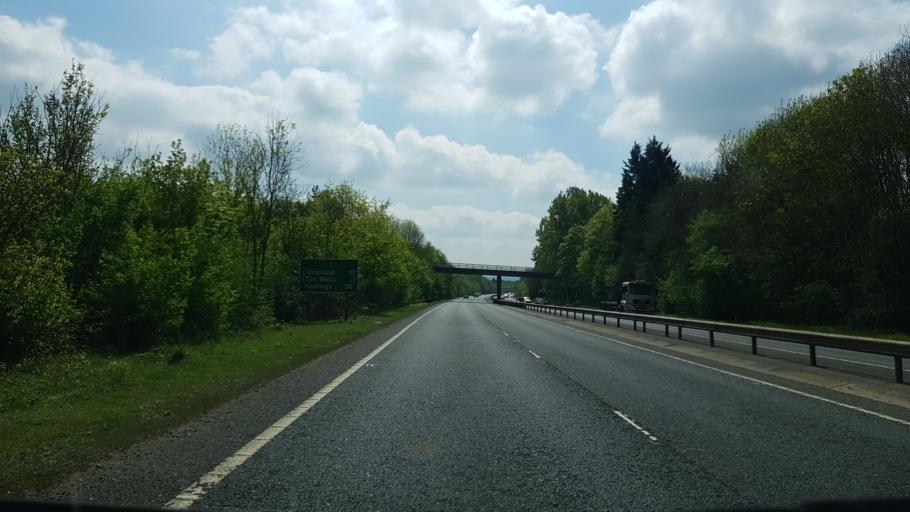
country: GB
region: England
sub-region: Kent
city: Sevenoaks
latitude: 51.2334
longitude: 0.2151
